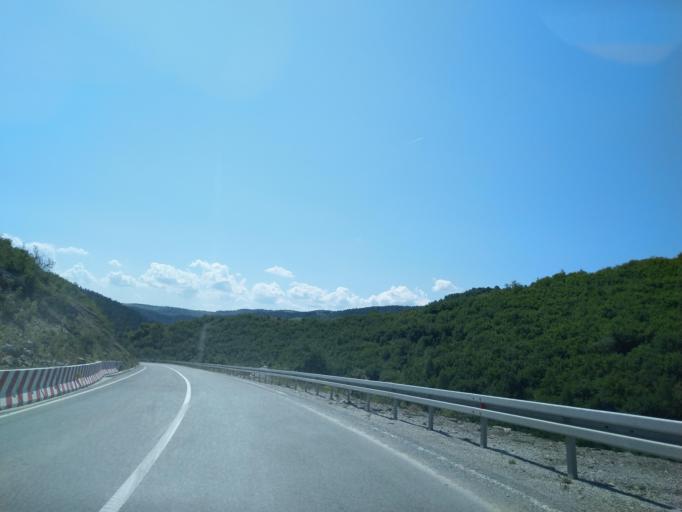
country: RS
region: Central Serbia
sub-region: Zlatiborski Okrug
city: Sjenica
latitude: 43.2966
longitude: 19.9364
